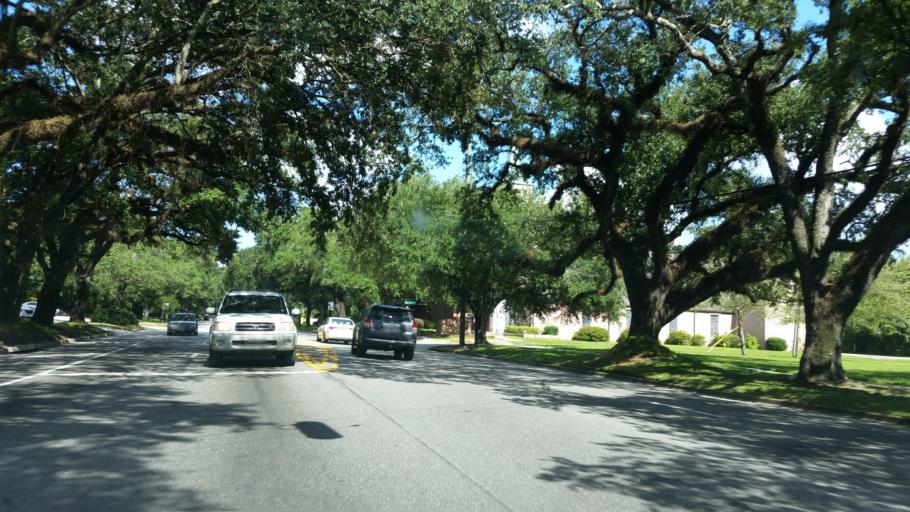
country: US
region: Alabama
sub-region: Mobile County
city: Mobile
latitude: 30.6779
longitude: -88.0812
